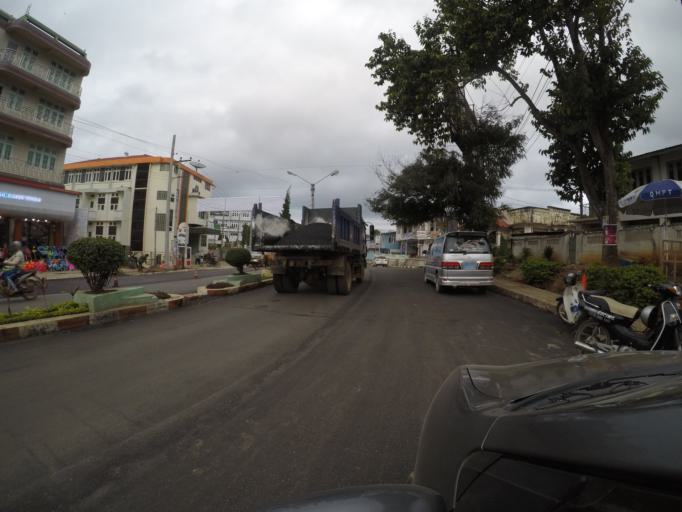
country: MM
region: Shan
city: Taunggyi
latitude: 20.7915
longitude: 97.0371
